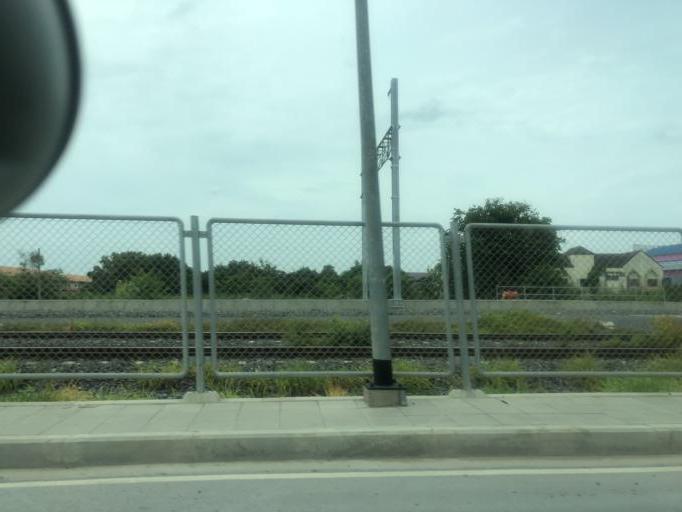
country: TH
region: Bangkok
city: Don Mueang
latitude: 13.9489
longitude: 100.6072
